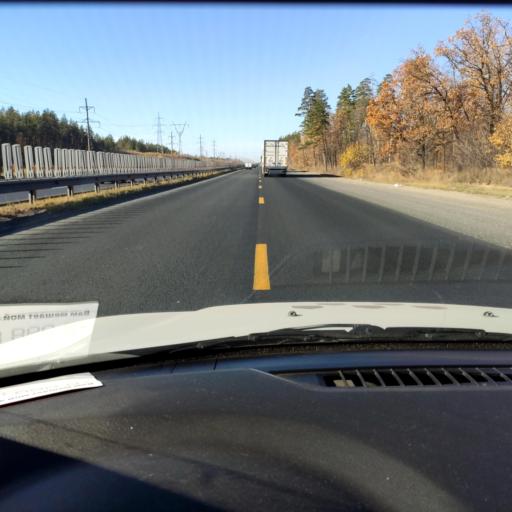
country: RU
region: Samara
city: Pribrezhnyy
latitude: 53.5140
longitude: 49.8988
